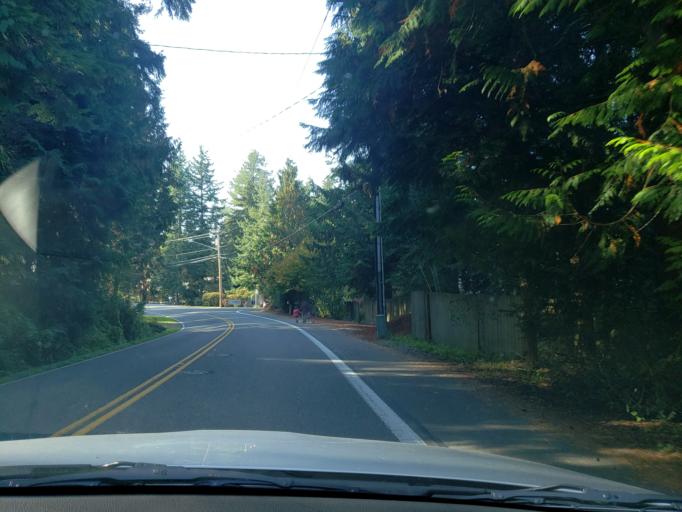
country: US
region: Washington
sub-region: Snohomish County
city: Meadowdale
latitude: 47.8646
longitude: -122.3150
